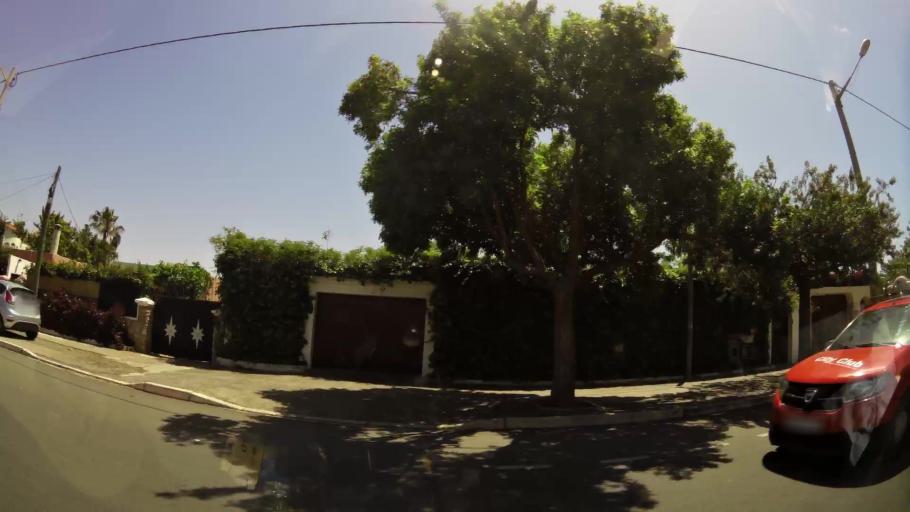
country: MA
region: Souss-Massa-Draa
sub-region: Agadir-Ida-ou-Tnan
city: Agadir
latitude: 30.4315
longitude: -9.5948
